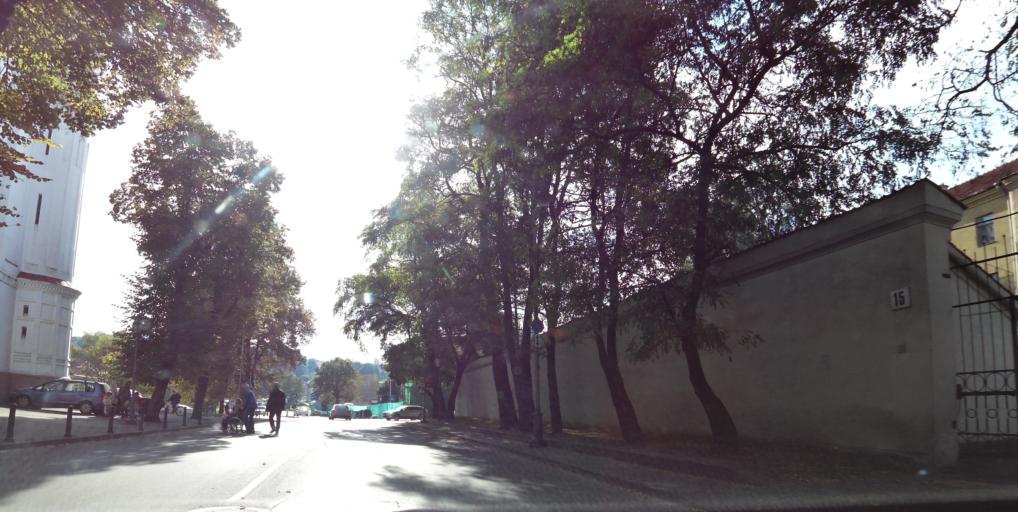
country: LT
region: Vilnius County
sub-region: Vilnius
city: Vilnius
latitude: 54.6812
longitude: 25.2917
